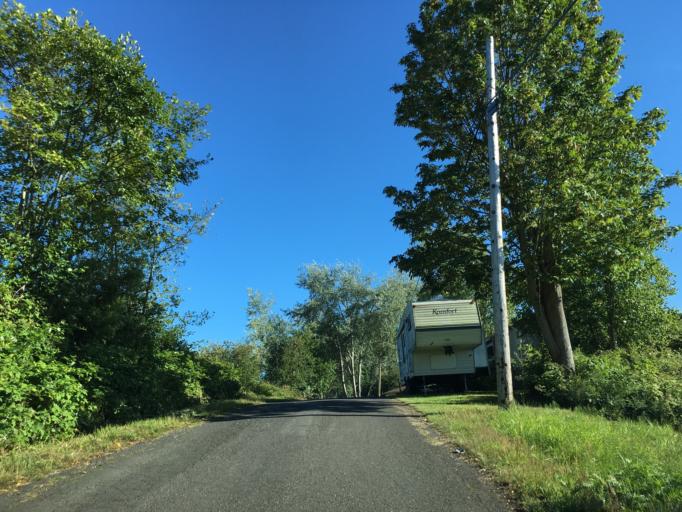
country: US
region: Washington
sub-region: Whatcom County
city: Birch Bay
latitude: 48.9160
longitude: -122.7431
